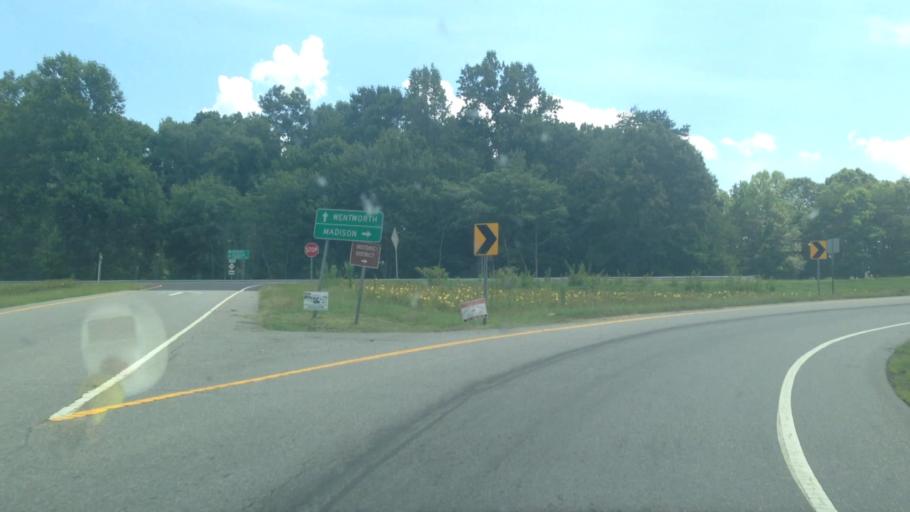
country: US
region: North Carolina
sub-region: Rockingham County
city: Madison
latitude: 36.3753
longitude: -79.9406
